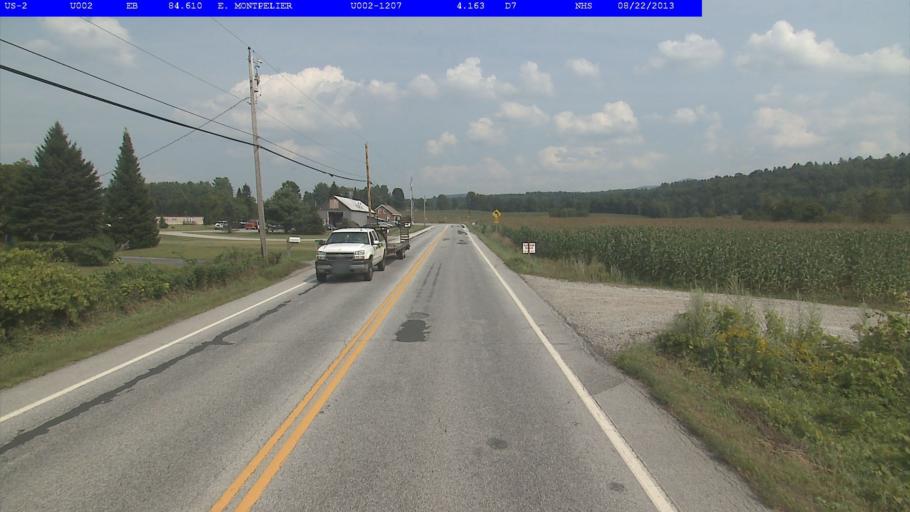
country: US
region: Vermont
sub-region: Washington County
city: Barre
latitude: 44.2690
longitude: -72.4629
